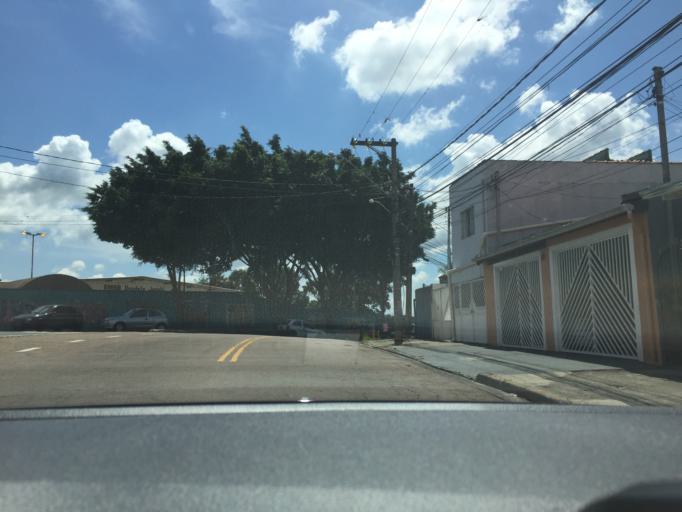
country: BR
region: Sao Paulo
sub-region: Jundiai
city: Jundiai
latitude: -23.1734
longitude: -46.8707
